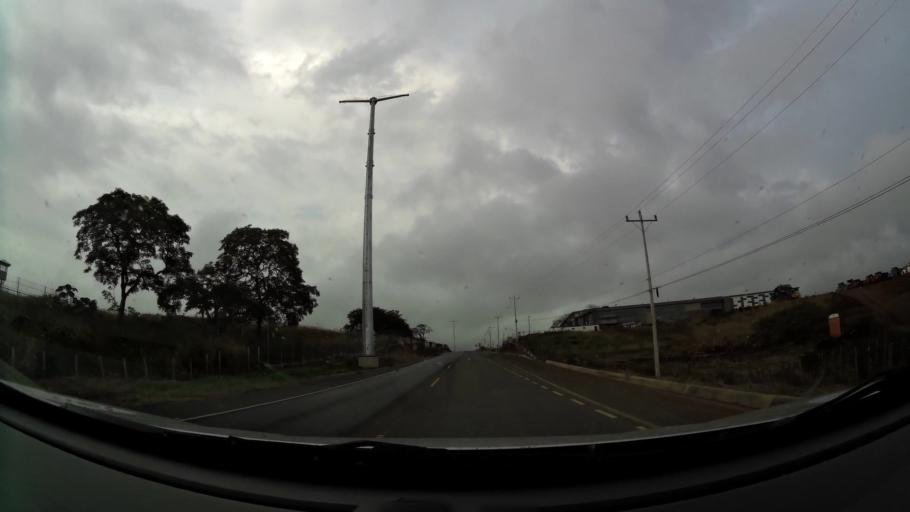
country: CR
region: Alajuela
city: Carrillos
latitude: 9.9739
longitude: -84.2776
